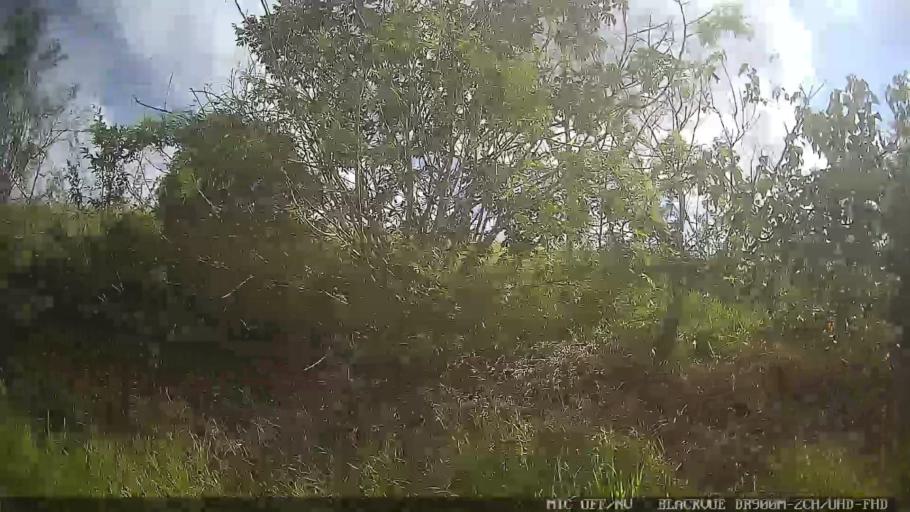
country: BR
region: Sao Paulo
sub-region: Atibaia
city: Atibaia
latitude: -23.0725
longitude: -46.5769
